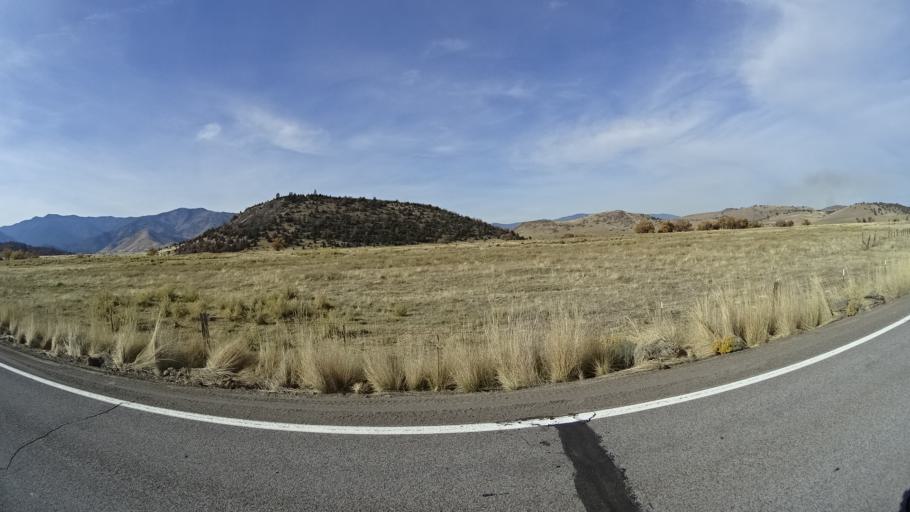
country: US
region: California
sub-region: Siskiyou County
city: Weed
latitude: 41.4827
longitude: -122.4098
